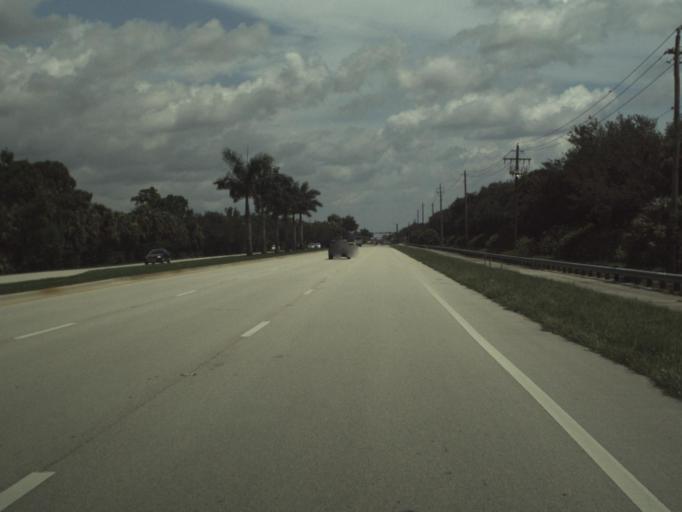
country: US
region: Florida
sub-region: Palm Beach County
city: Jupiter
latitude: 26.9163
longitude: -80.0940
